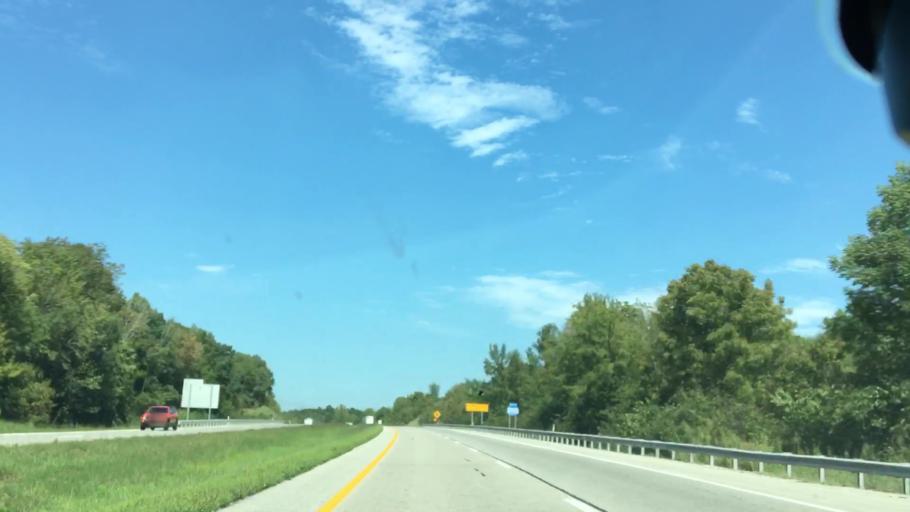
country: US
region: Kentucky
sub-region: Hopkins County
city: Nortonville
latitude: 37.1971
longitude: -87.4399
